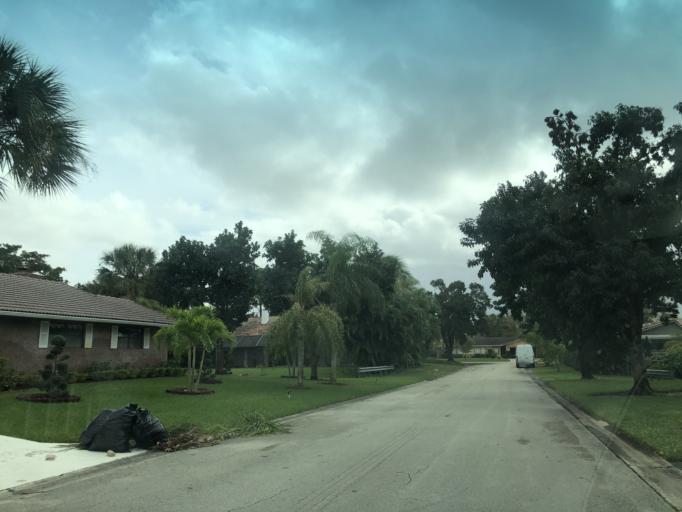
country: US
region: Florida
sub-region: Broward County
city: Margate
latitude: 26.2499
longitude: -80.2362
